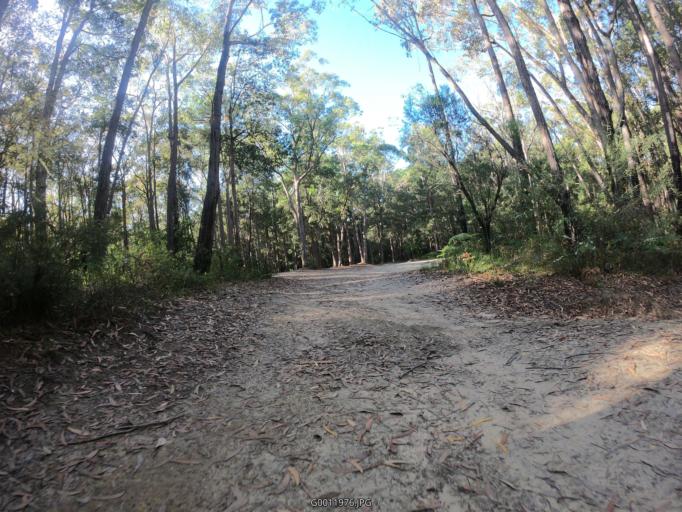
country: AU
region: New South Wales
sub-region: Lake Macquarie Shire
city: Cooranbong
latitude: -33.0677
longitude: 151.3389
